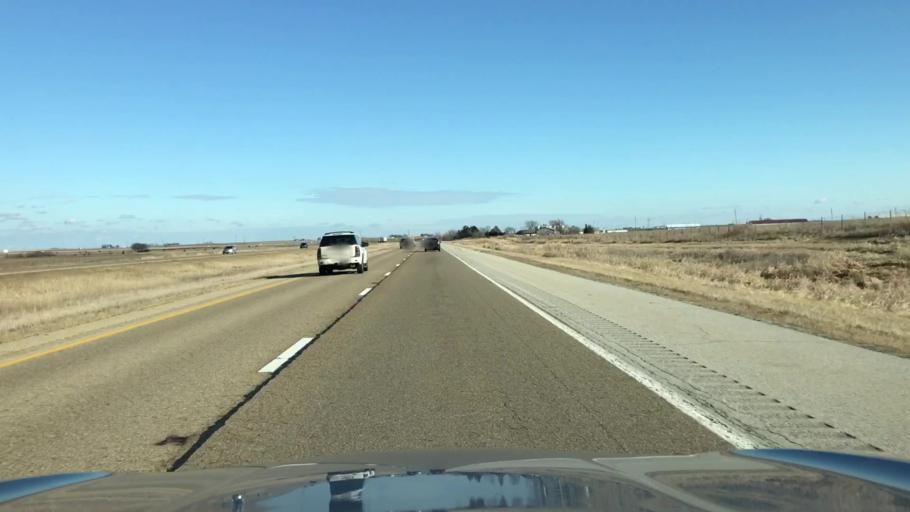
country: US
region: Illinois
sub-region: McLean County
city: Lexington
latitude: 40.6589
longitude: -88.7841
